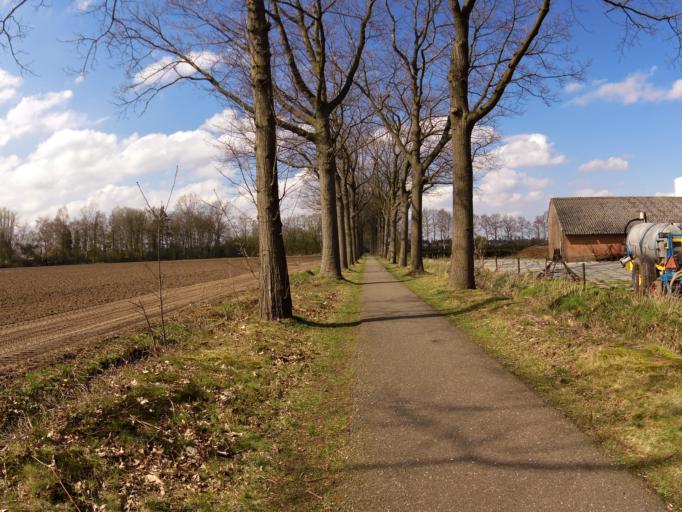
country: NL
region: North Brabant
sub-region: Gemeente Boxtel
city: Boxtel
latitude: 51.6076
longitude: 5.2989
